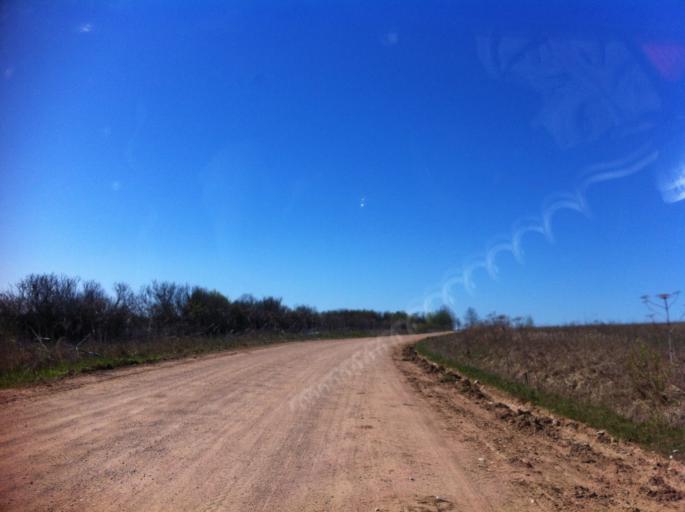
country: RU
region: Pskov
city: Izborsk
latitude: 57.8023
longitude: 27.9713
